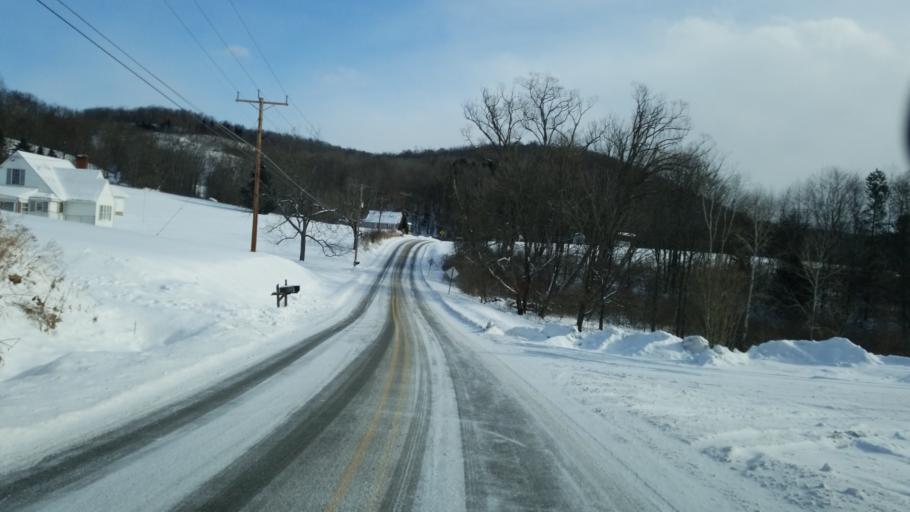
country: US
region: Pennsylvania
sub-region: Clearfield County
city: Hyde
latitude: 41.0156
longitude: -78.4609
